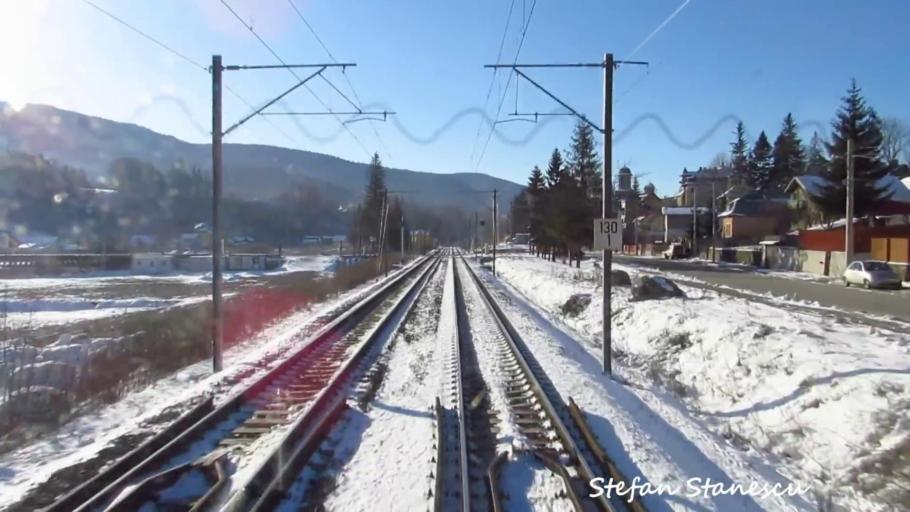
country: RO
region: Prahova
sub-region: Oras Busteni
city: Poiana Tapului
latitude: 45.3865
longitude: 25.5406
